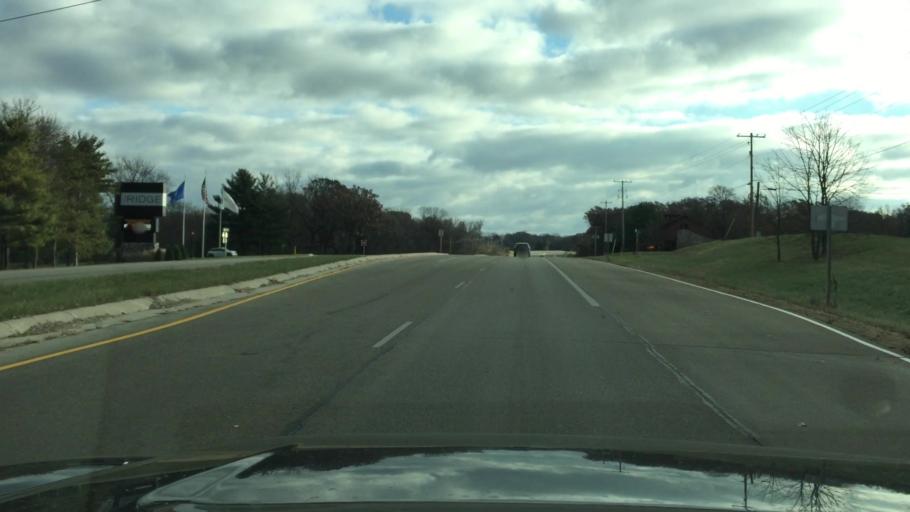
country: US
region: Wisconsin
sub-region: Walworth County
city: Williams Bay
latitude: 42.5830
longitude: -88.5103
